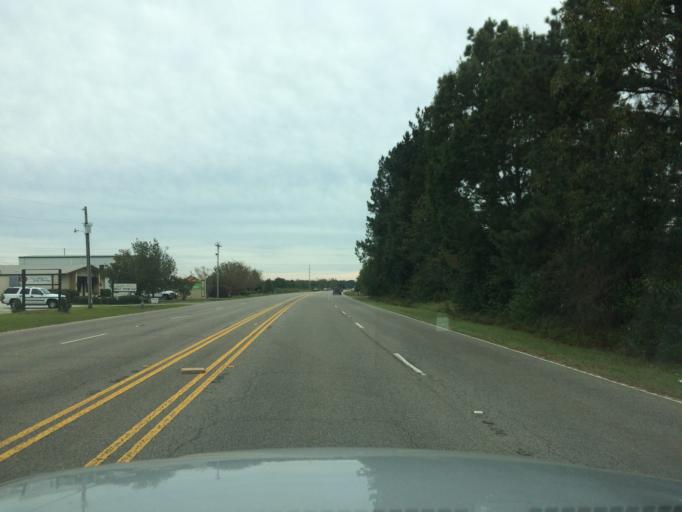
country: US
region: South Carolina
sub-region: Aiken County
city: New Ellenton
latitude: 33.4620
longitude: -81.6874
